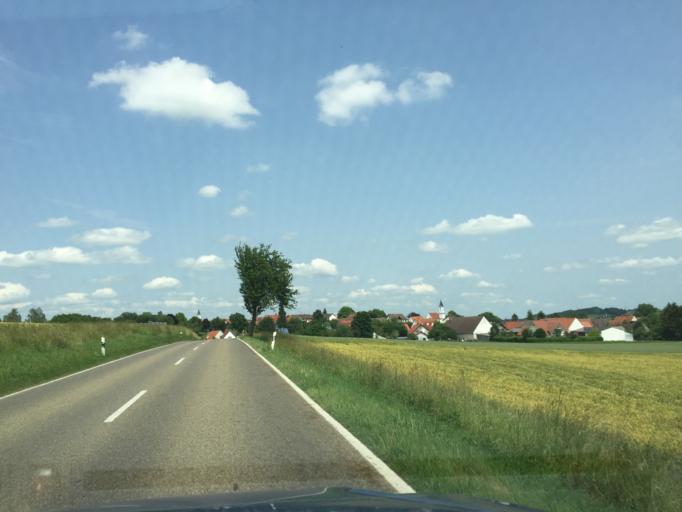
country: DE
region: Bavaria
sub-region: Swabia
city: Zusamaltheim
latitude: 48.5210
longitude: 10.6286
